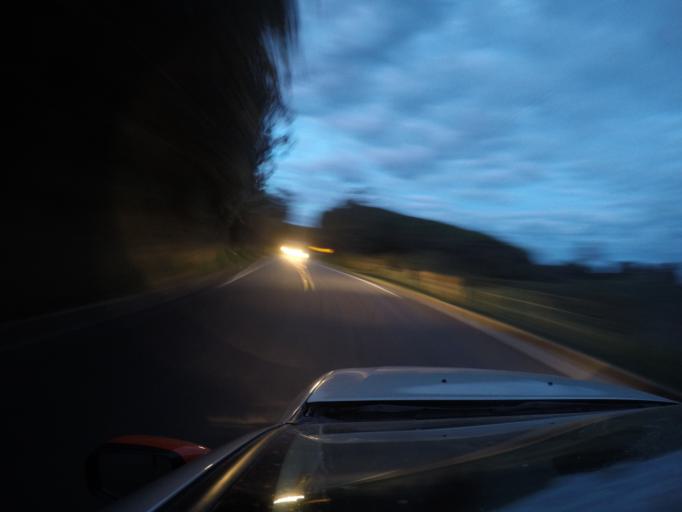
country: CO
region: Tolima
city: Casabianca
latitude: 5.1418
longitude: -75.1169
